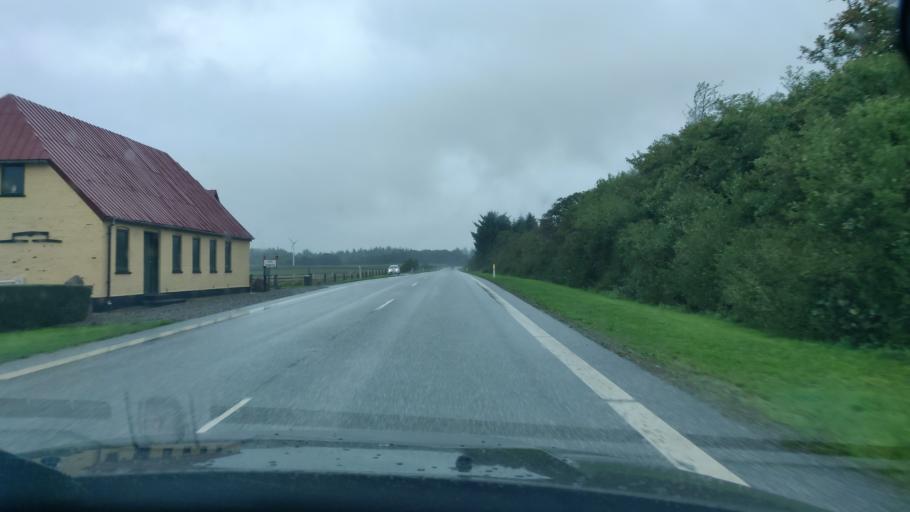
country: DK
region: North Denmark
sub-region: Thisted Kommune
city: Hurup
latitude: 56.8300
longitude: 8.5045
